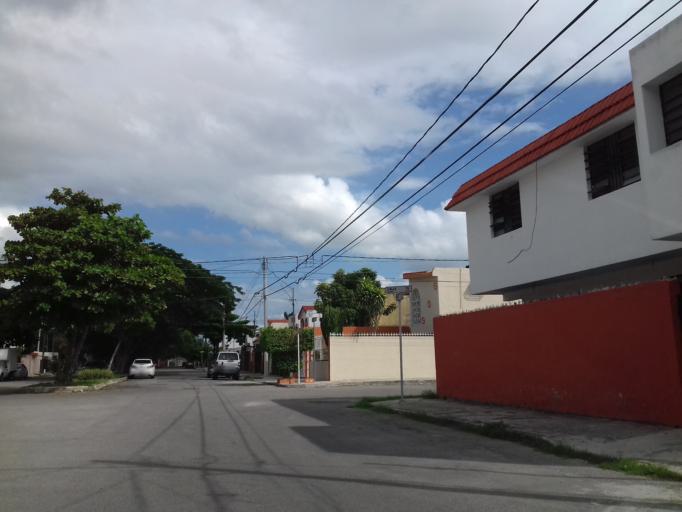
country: MX
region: Yucatan
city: Merida
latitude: 21.0063
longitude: -89.6082
